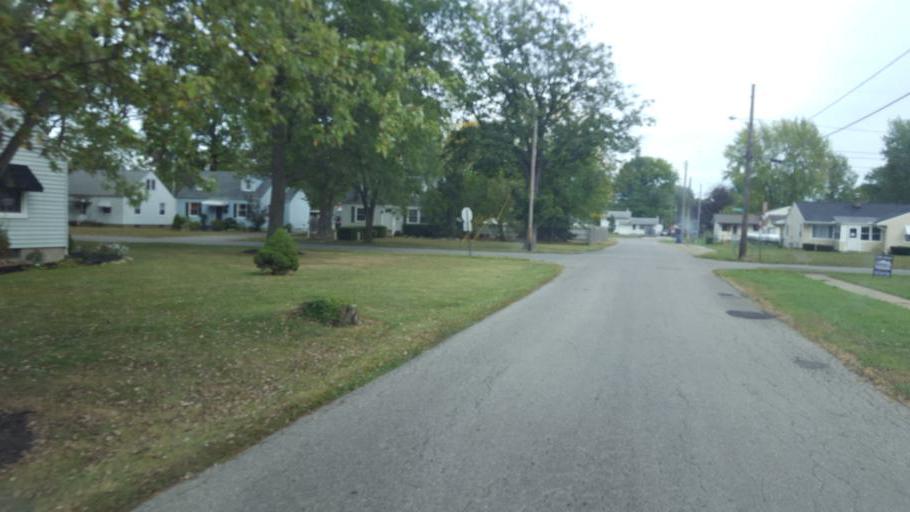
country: US
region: Ohio
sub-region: Lorain County
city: Sheffield Lake
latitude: 41.4827
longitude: -82.1214
